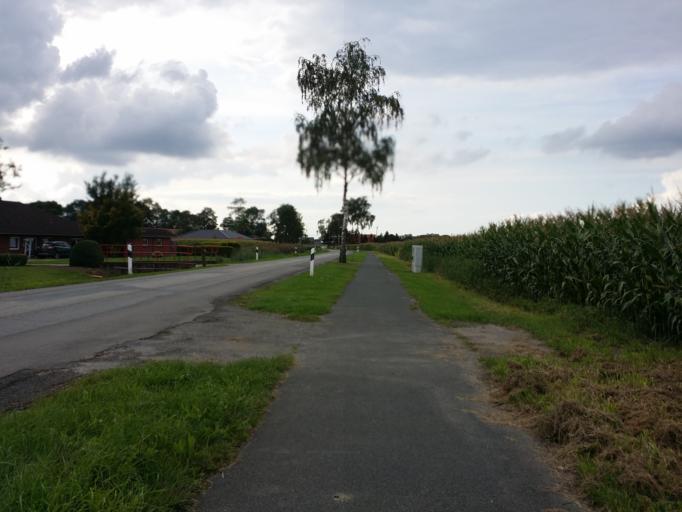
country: DE
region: Lower Saxony
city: Oederquart
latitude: 53.7845
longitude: 9.2391
